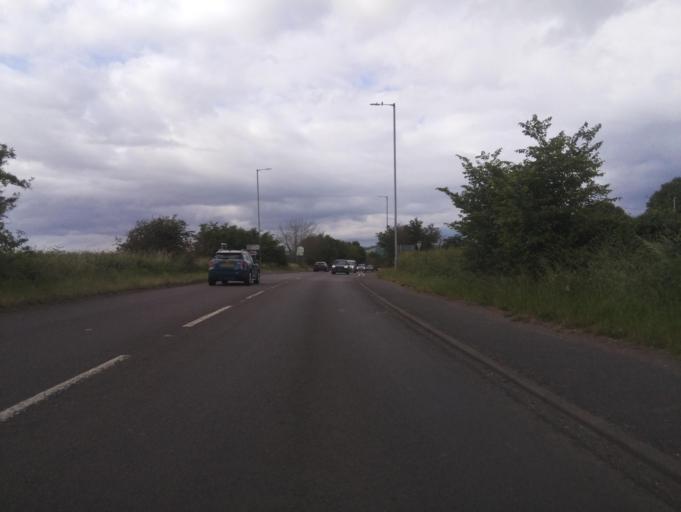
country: GB
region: England
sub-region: Dudley
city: Kingswinford
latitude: 52.4942
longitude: -2.1887
